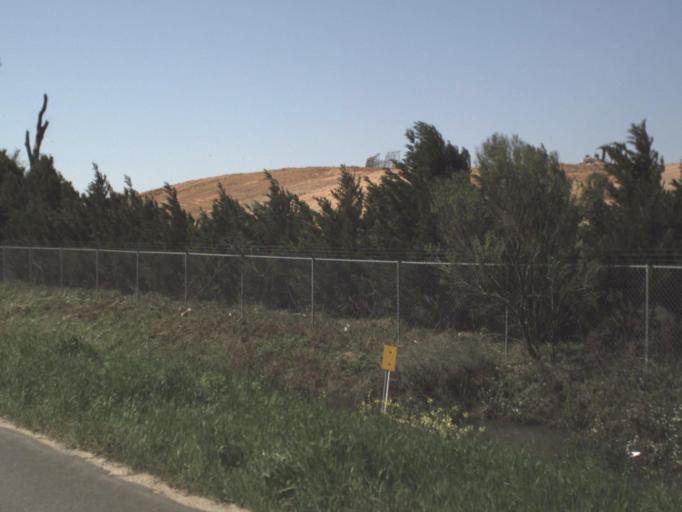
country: US
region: Florida
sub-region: Jackson County
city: Graceville
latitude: 30.9203
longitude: -85.4288
